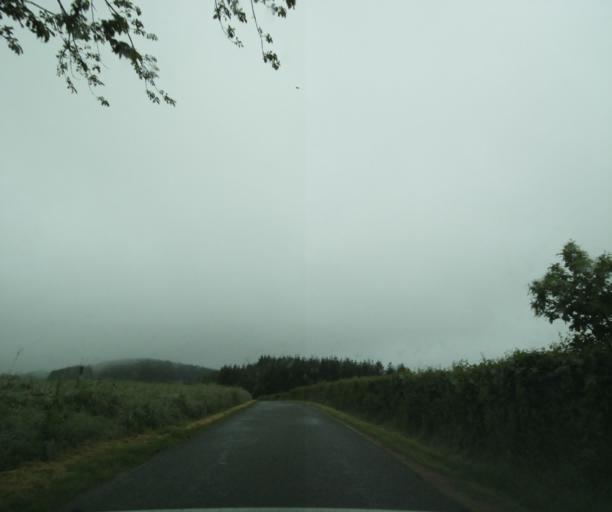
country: FR
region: Bourgogne
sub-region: Departement de Saone-et-Loire
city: Charolles
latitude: 46.4044
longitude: 4.3783
